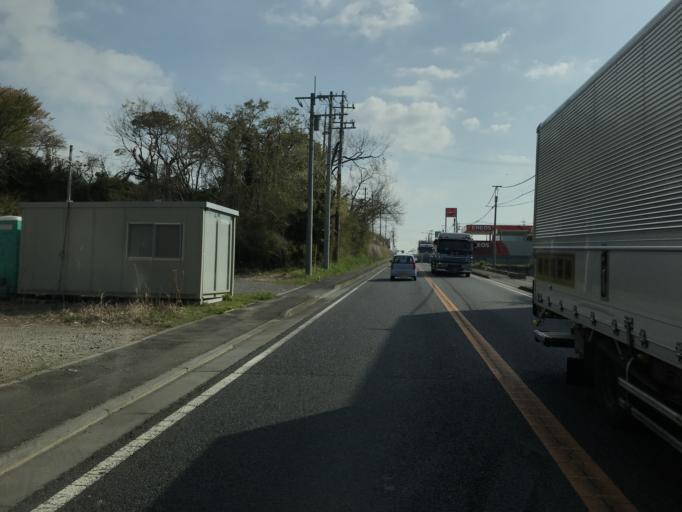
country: JP
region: Chiba
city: Narita
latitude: 35.8138
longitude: 140.3904
